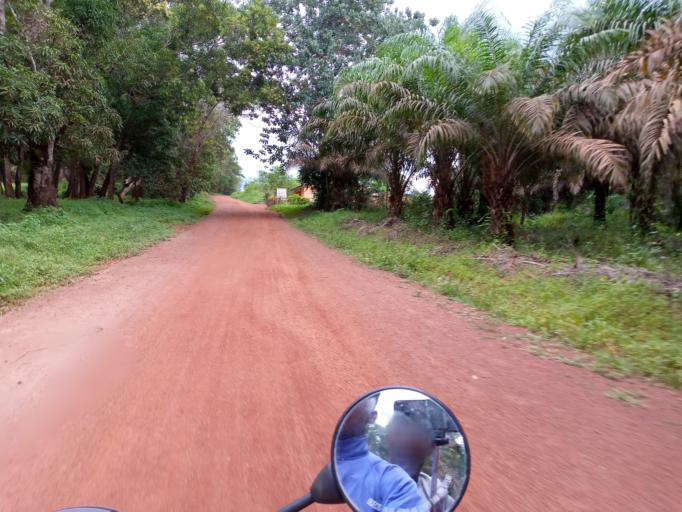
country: SL
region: Northern Province
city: Mange
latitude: 8.8998
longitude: -12.7201
